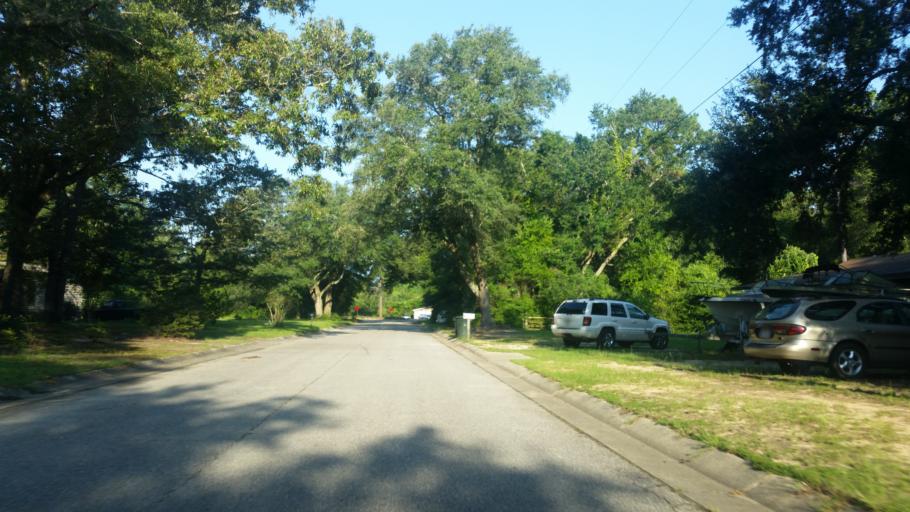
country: US
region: Florida
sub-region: Escambia County
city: Ensley
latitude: 30.5258
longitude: -87.3243
